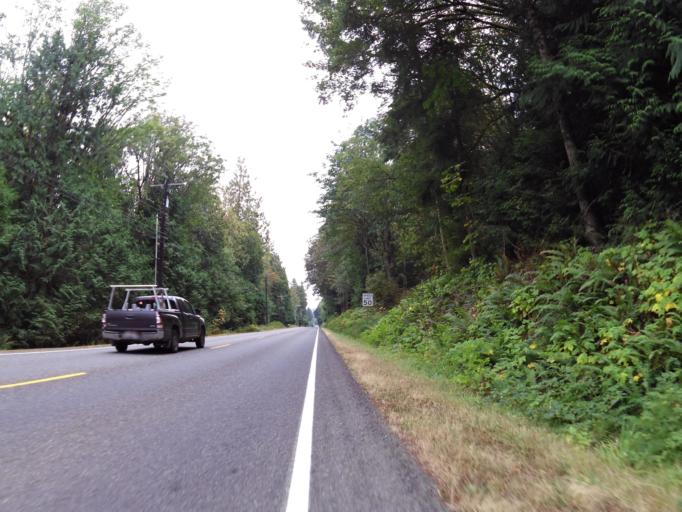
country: US
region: Washington
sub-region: Jefferson County
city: Port Hadlock-Irondale
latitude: 47.9995
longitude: -122.7239
